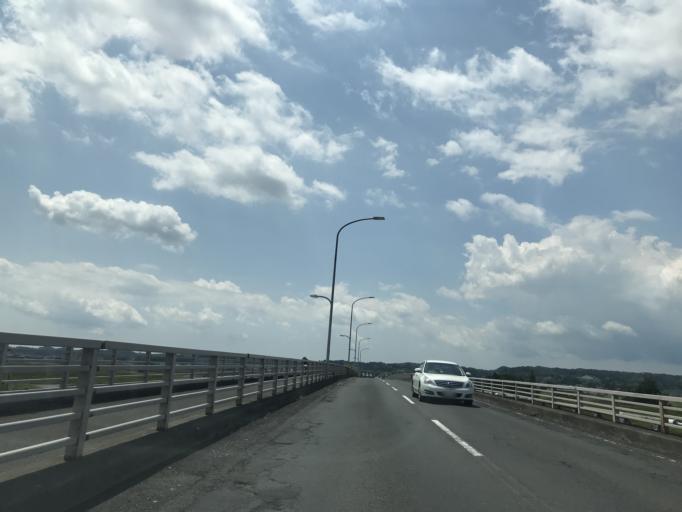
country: JP
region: Miyagi
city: Kogota
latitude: 38.5285
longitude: 141.0581
